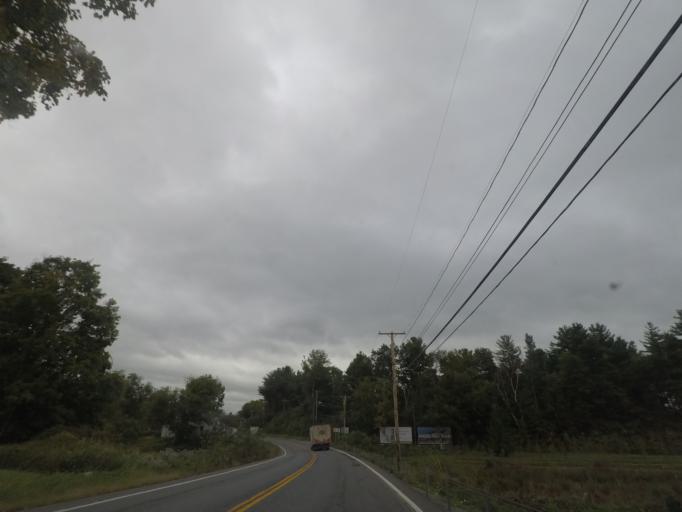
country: US
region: New York
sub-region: Rensselaer County
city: Hoosick Falls
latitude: 42.9317
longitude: -73.3579
